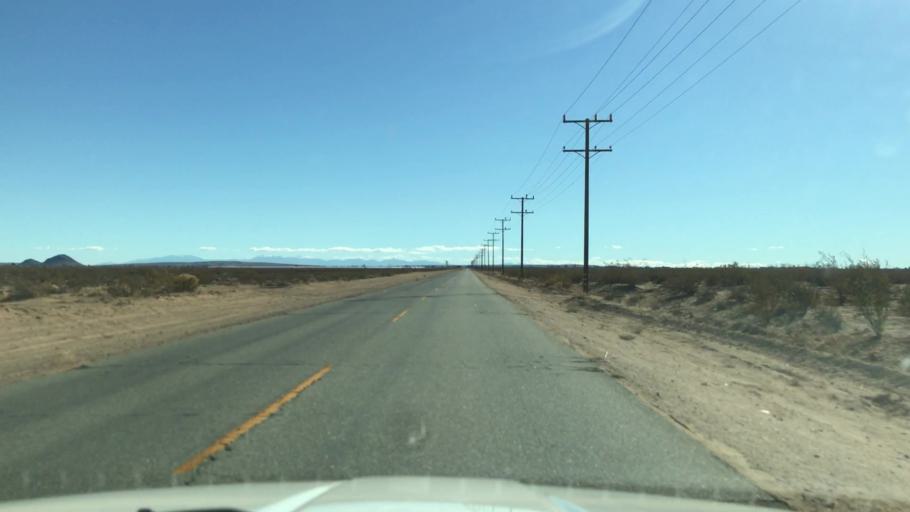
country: US
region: California
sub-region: Kern County
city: California City
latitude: 35.1699
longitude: -117.9858
